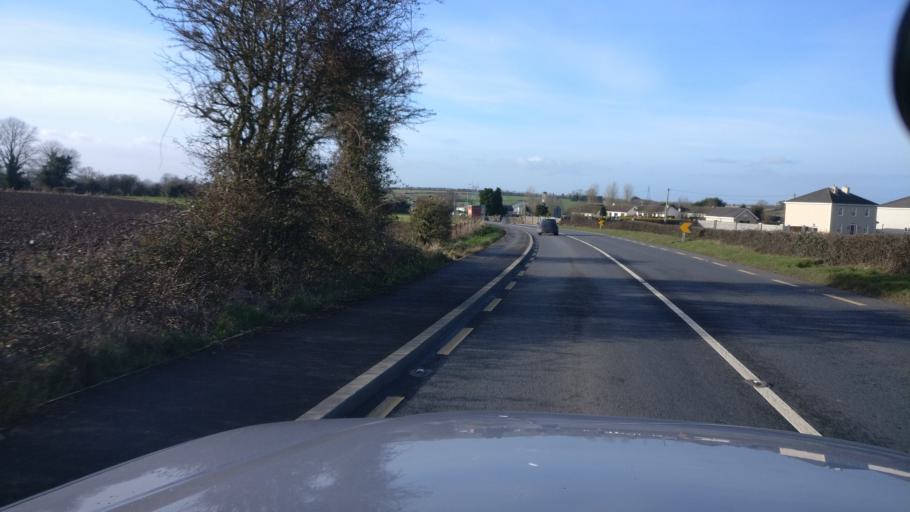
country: IE
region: Leinster
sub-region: Uibh Fhaili
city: Tullamore
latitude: 53.2123
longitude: -7.4425
